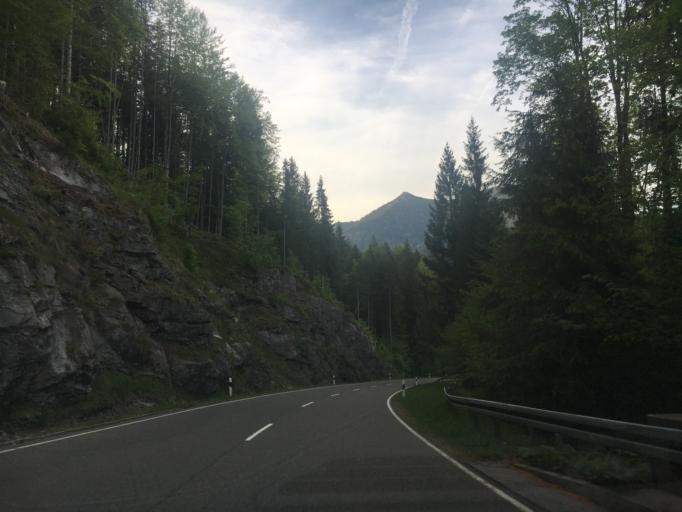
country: DE
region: Bavaria
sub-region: Upper Bavaria
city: Wallgau
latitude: 47.5805
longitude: 11.3041
